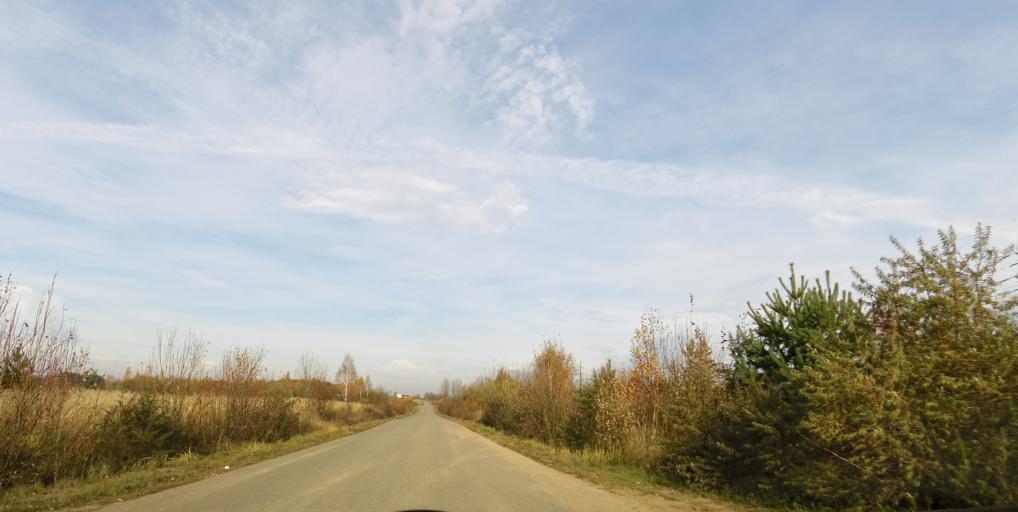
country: LT
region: Vilnius County
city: Justiniskes
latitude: 54.7075
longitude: 25.2061
